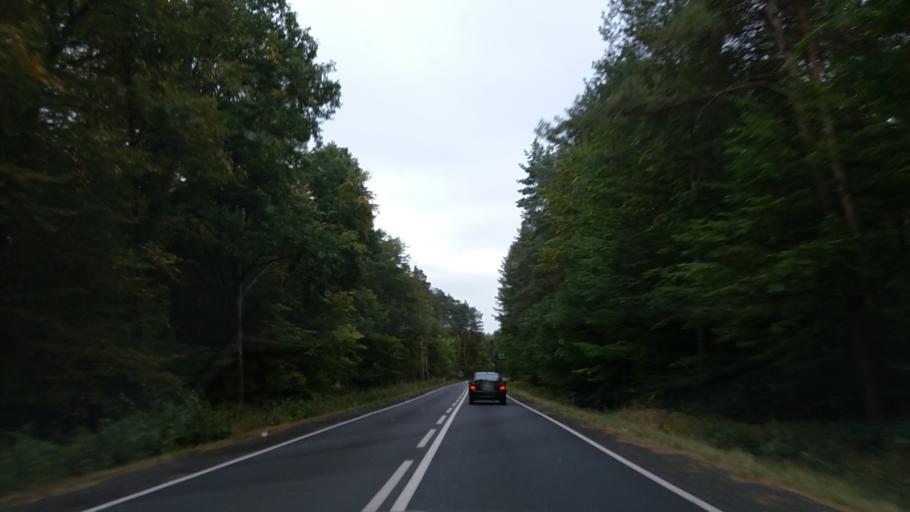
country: PL
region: Lubusz
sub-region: Powiat gorzowski
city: Klodawa
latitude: 52.8751
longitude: 15.2007
